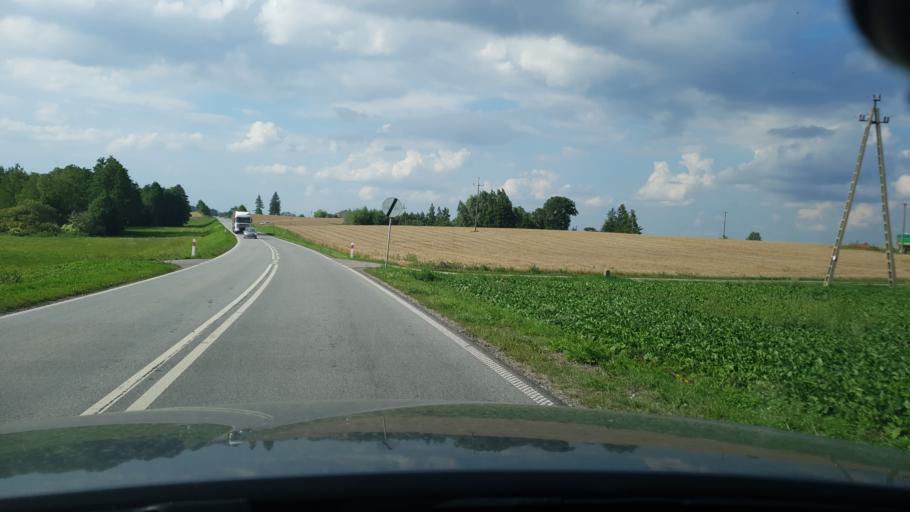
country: PL
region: Kujawsko-Pomorskie
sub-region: Powiat grudziadzki
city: Radzyn Chelminski
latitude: 53.3359
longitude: 18.9370
